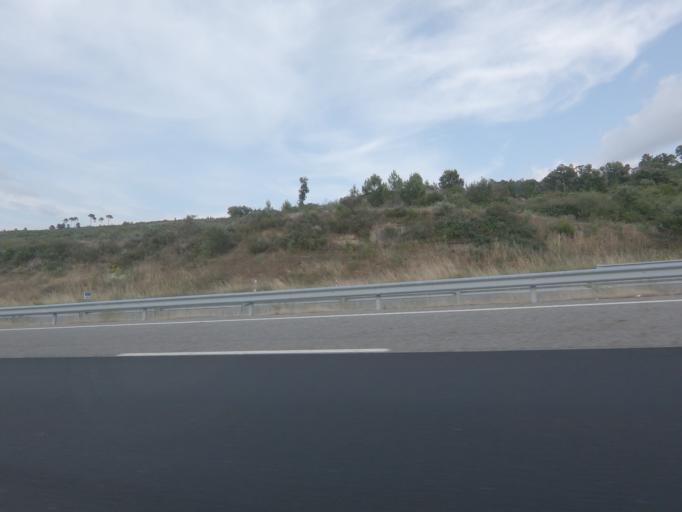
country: PT
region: Vila Real
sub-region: Boticas
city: Boticas
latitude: 41.6260
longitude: -7.5964
